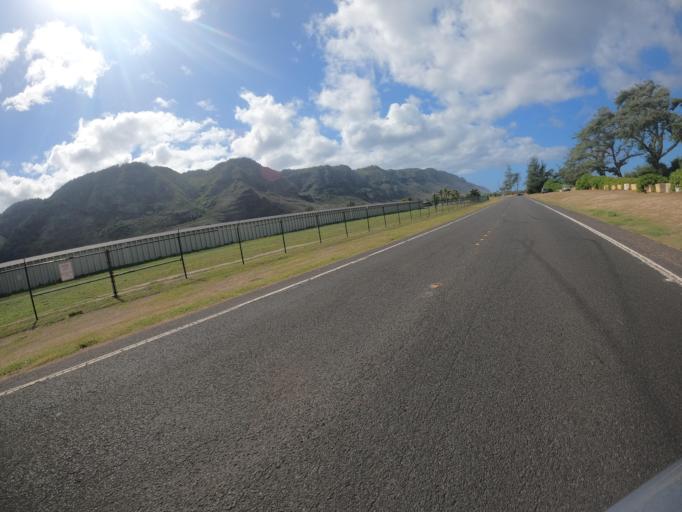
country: US
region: Hawaii
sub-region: Honolulu County
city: Mokuleia
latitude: 21.5838
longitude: -158.2070
